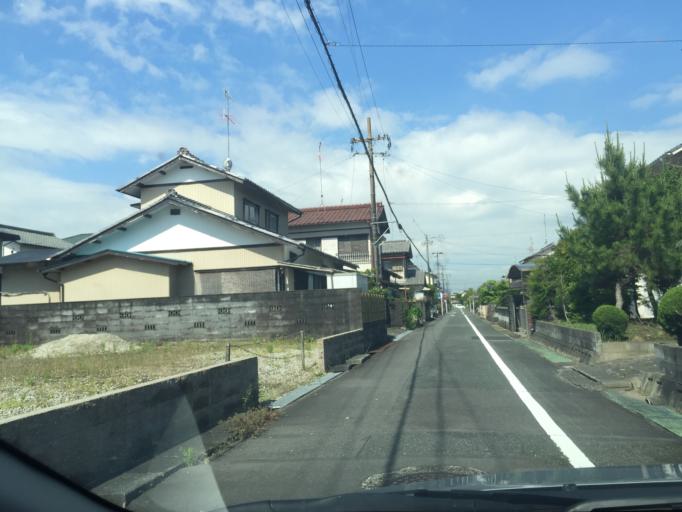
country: JP
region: Shizuoka
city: Kakegawa
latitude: 34.7776
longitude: 138.0059
